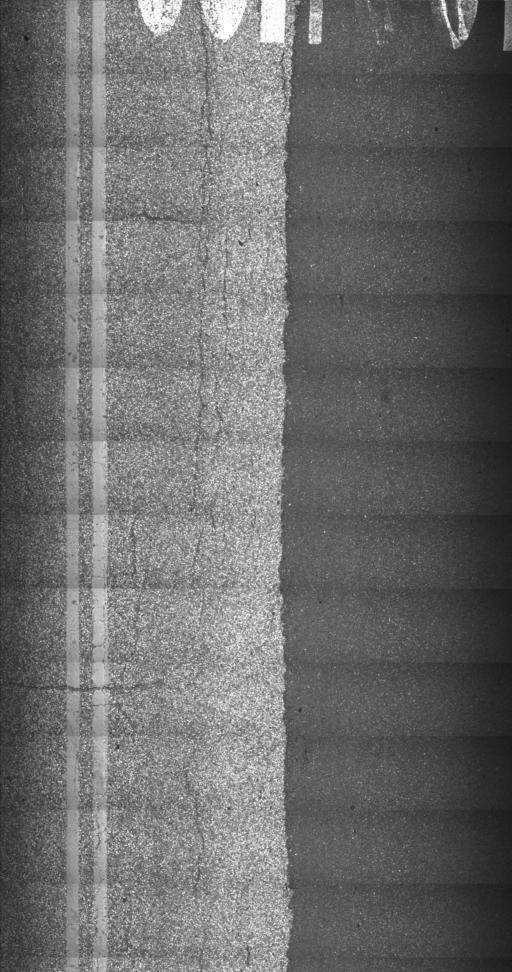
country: US
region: Vermont
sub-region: Windsor County
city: Woodstock
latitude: 43.6203
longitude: -72.5181
